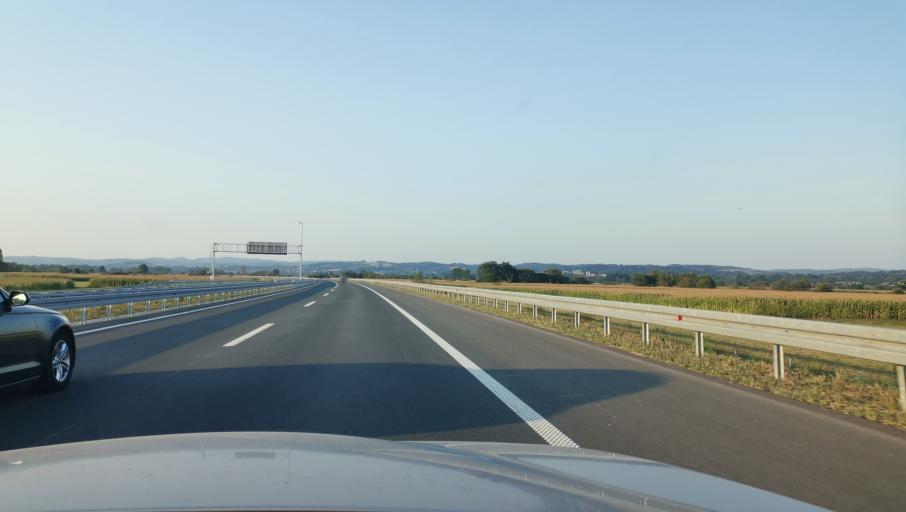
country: RS
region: Central Serbia
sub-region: Kolubarski Okrug
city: Ljig
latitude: 44.2476
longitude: 20.2675
